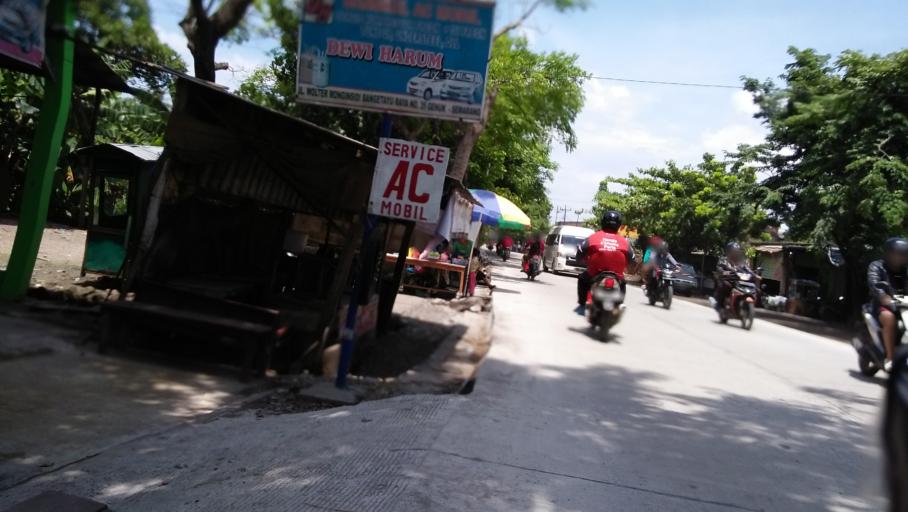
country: ID
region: Central Java
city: Mranggen
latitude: -6.9815
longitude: 110.4799
